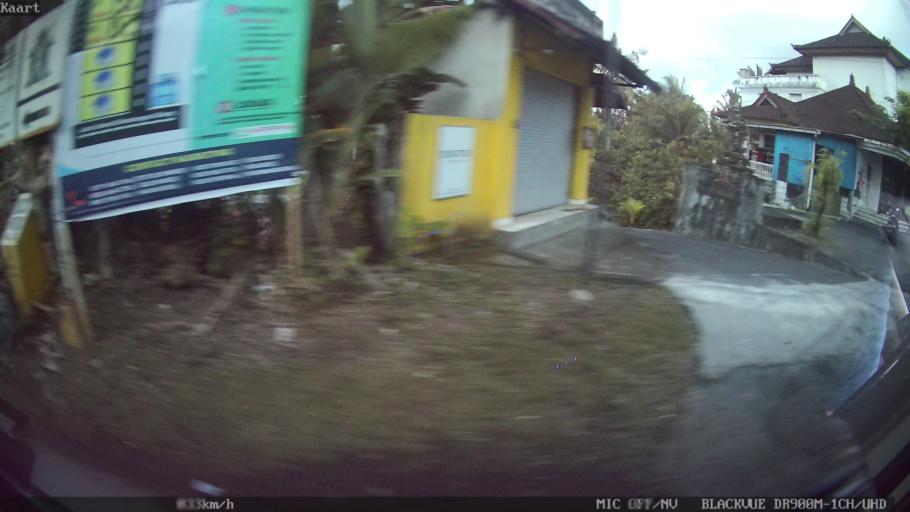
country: ID
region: Bali
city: Banjar Mambalkajanan
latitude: -8.5604
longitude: 115.2193
